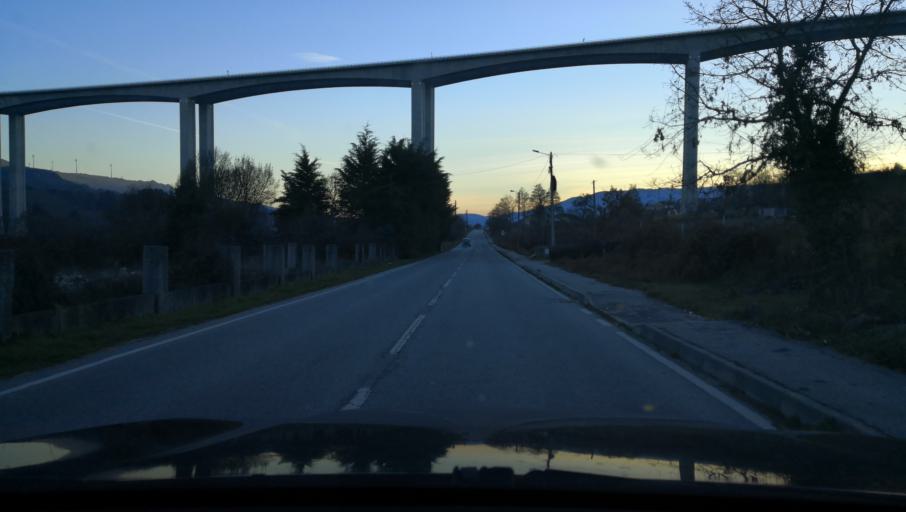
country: PT
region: Vila Real
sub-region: Vila Pouca de Aguiar
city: Vila Pouca de Aguiar
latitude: 41.4853
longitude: -7.6521
